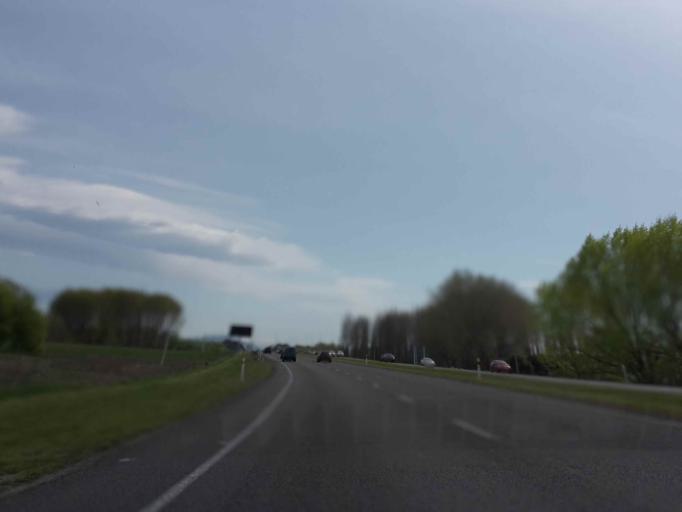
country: NZ
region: Canterbury
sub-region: Waimakariri District
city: Kaiapoi
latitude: -43.4217
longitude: 172.6484
